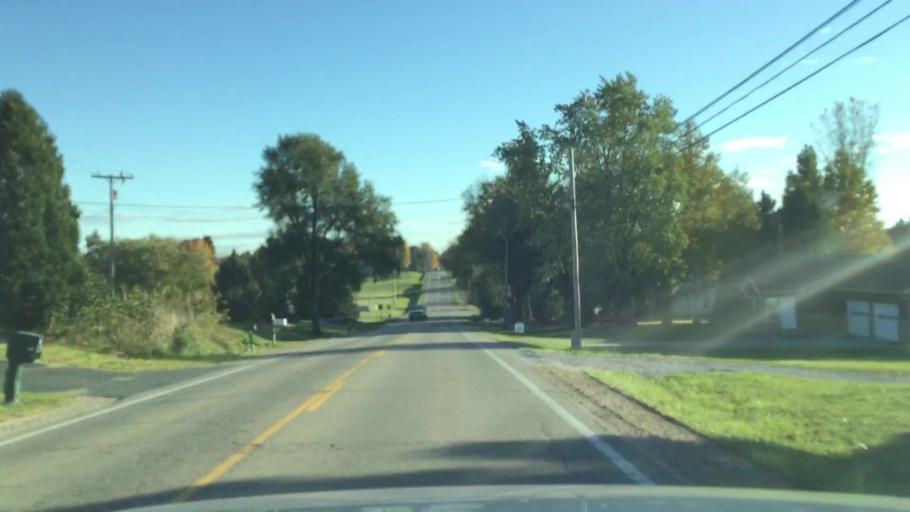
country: US
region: Michigan
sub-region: Lapeer County
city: Imlay City
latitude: 43.0363
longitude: -83.1668
